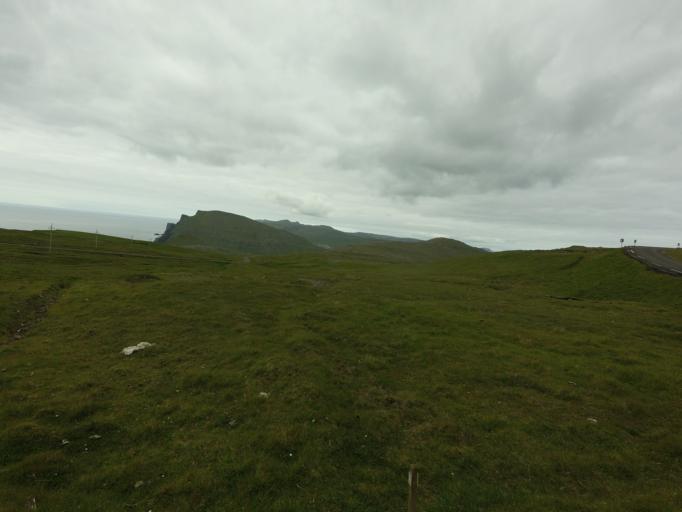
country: FO
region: Suduroy
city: Vagur
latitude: 61.4276
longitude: -6.7544
